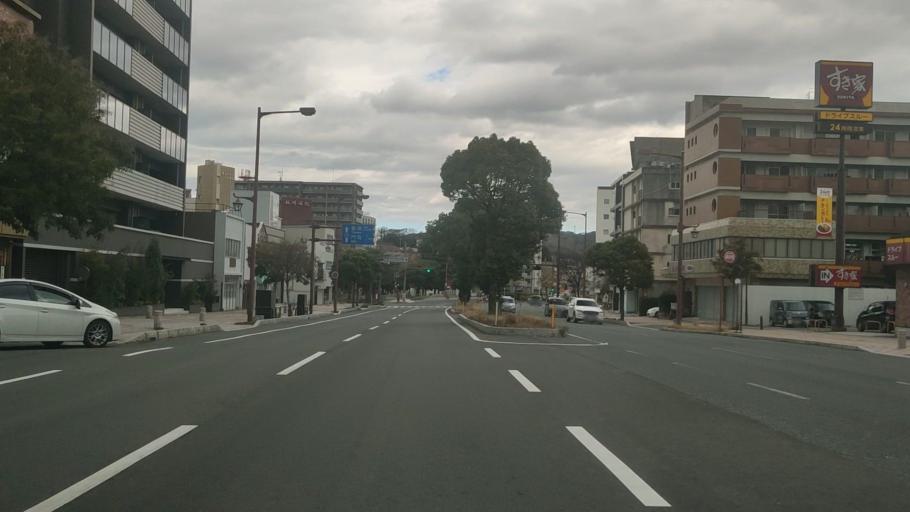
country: JP
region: Yamaguchi
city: Shimonoseki
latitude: 33.9593
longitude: 130.9420
